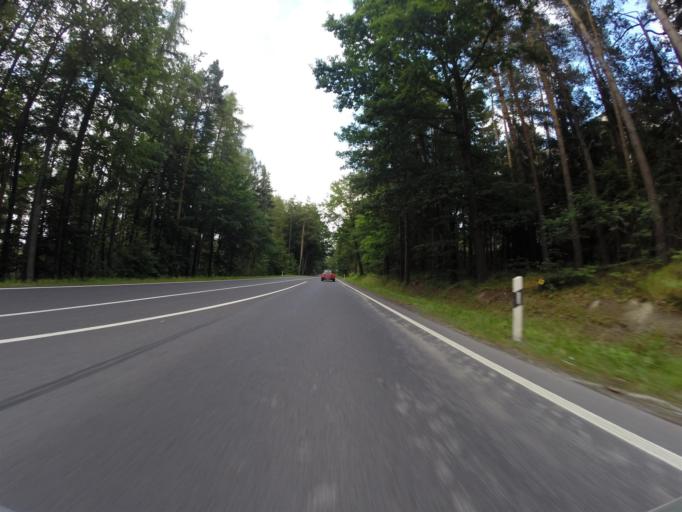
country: DE
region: Thuringia
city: Neuhaus
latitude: 50.6947
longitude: 10.9527
